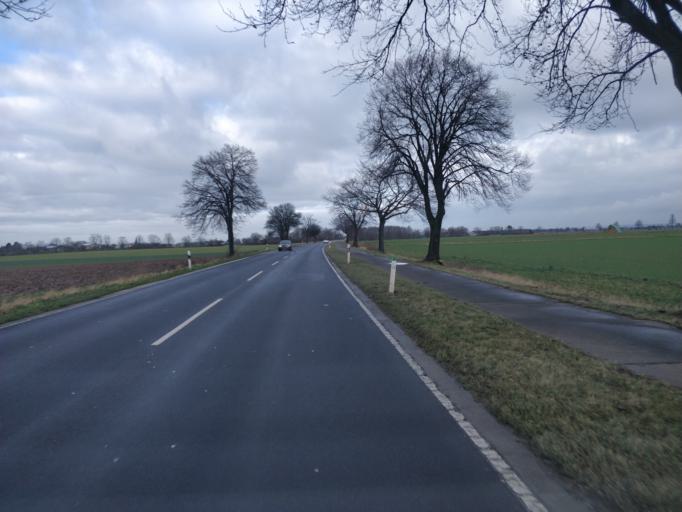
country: DE
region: North Rhine-Westphalia
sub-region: Regierungsbezirk Koln
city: Euskirchen
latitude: 50.6364
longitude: 6.8433
